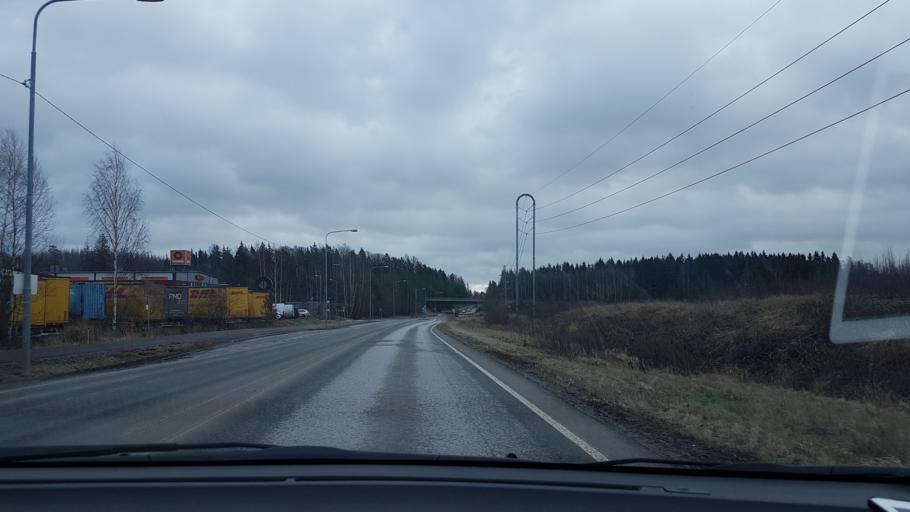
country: FI
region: Uusimaa
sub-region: Helsinki
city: Tuusula
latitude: 60.3794
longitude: 25.0493
